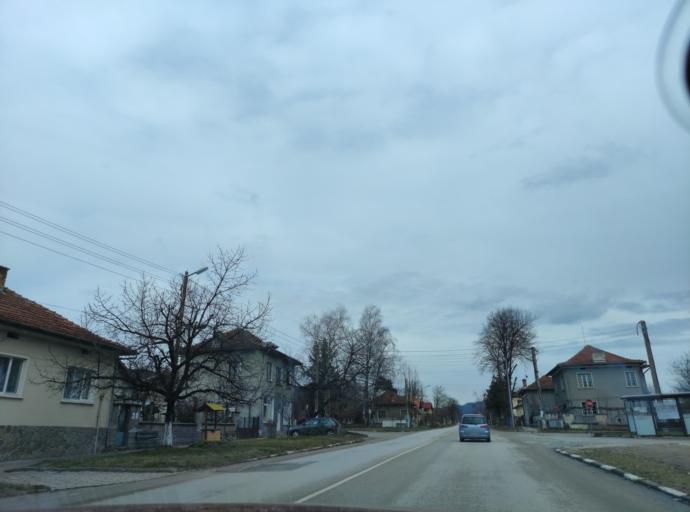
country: BG
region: Sofiya
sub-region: Obshtina Pravets
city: Pravets
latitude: 42.9129
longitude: 23.8717
